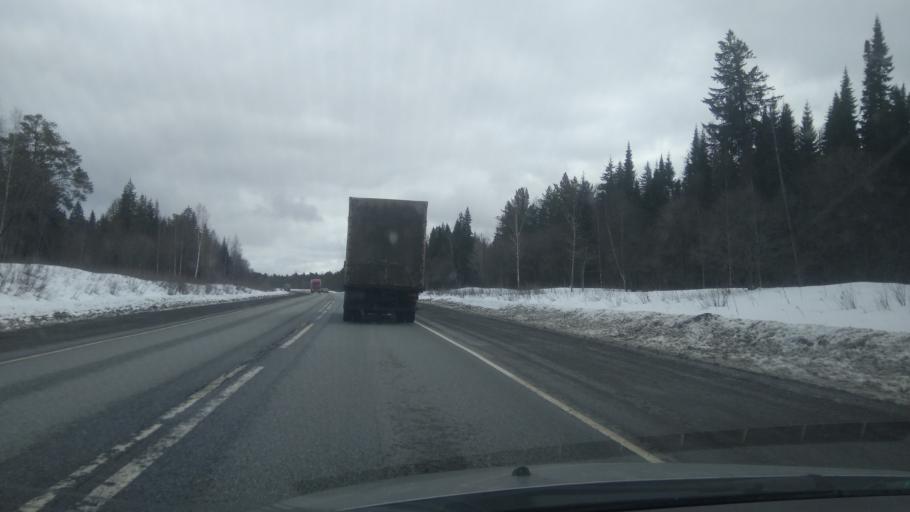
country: RU
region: Sverdlovsk
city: Atig
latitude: 56.7988
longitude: 59.3887
